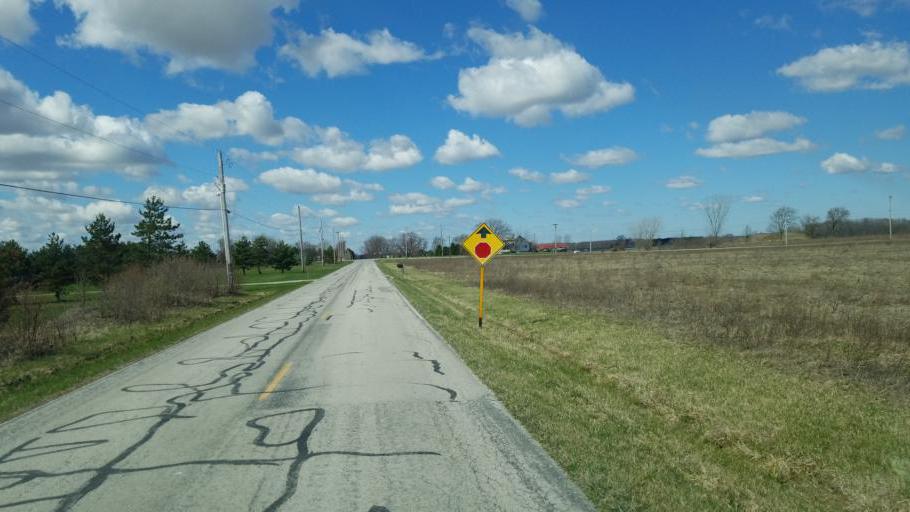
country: US
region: Ohio
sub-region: Sandusky County
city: Green Springs
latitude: 41.2419
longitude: -82.9986
